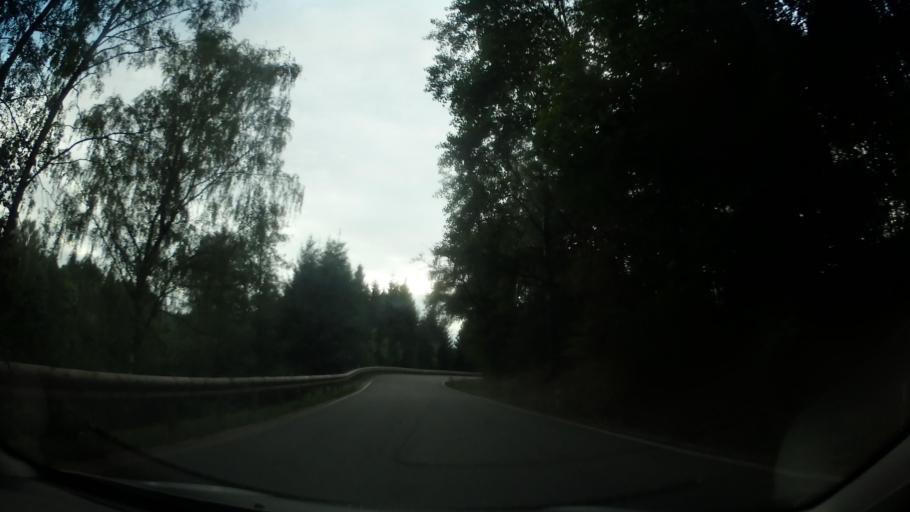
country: CZ
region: Pardubicky
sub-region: Okres Chrudim
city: Nasavrky
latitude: 49.7983
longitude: 15.7789
